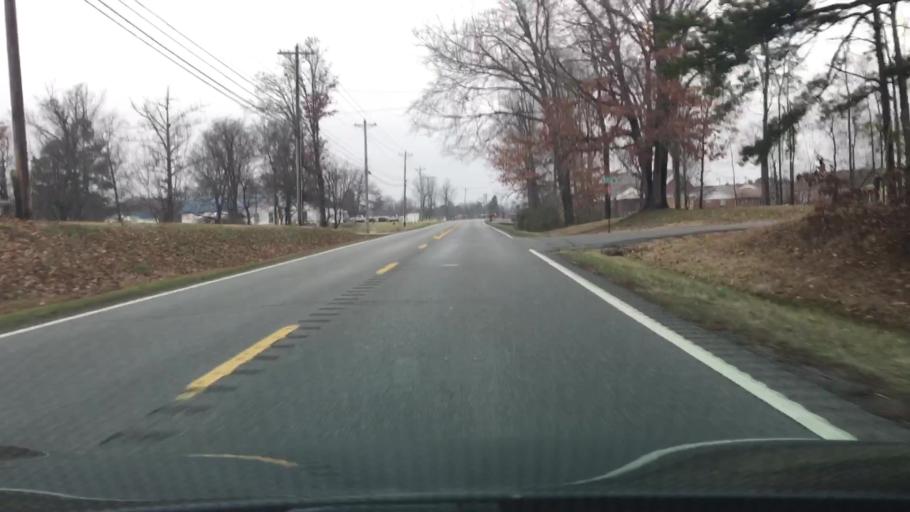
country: US
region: Kentucky
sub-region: Marshall County
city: Benton
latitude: 36.9407
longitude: -88.3607
